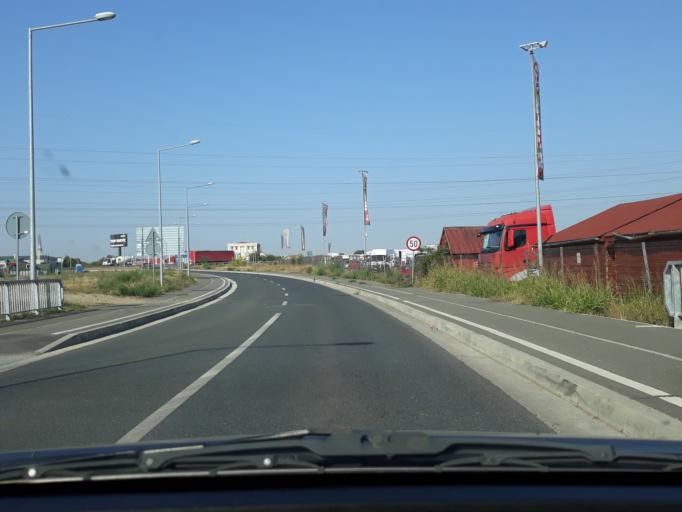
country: RO
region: Bihor
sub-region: Comuna Sanmartin
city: Sanmartin
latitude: 47.0295
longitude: 21.9433
